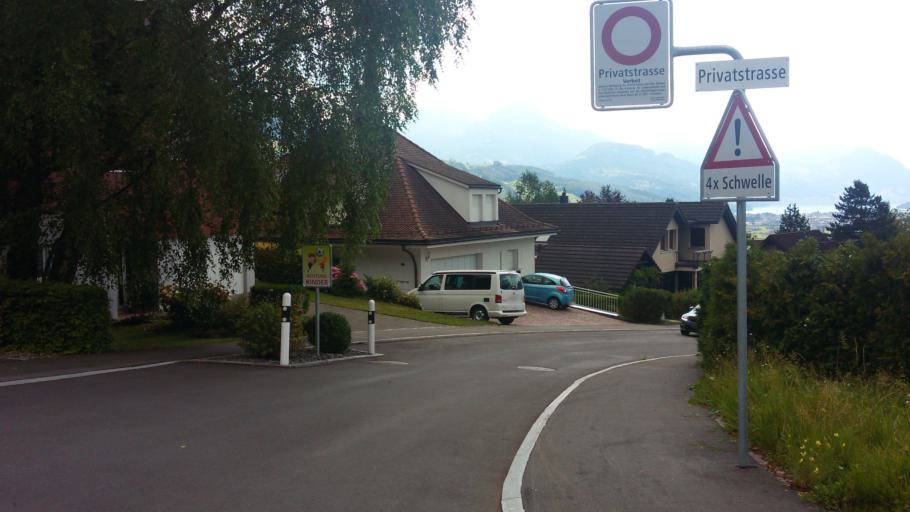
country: CH
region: Schwyz
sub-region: Bezirk Schwyz
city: Schwyz
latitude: 47.0176
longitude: 8.6647
